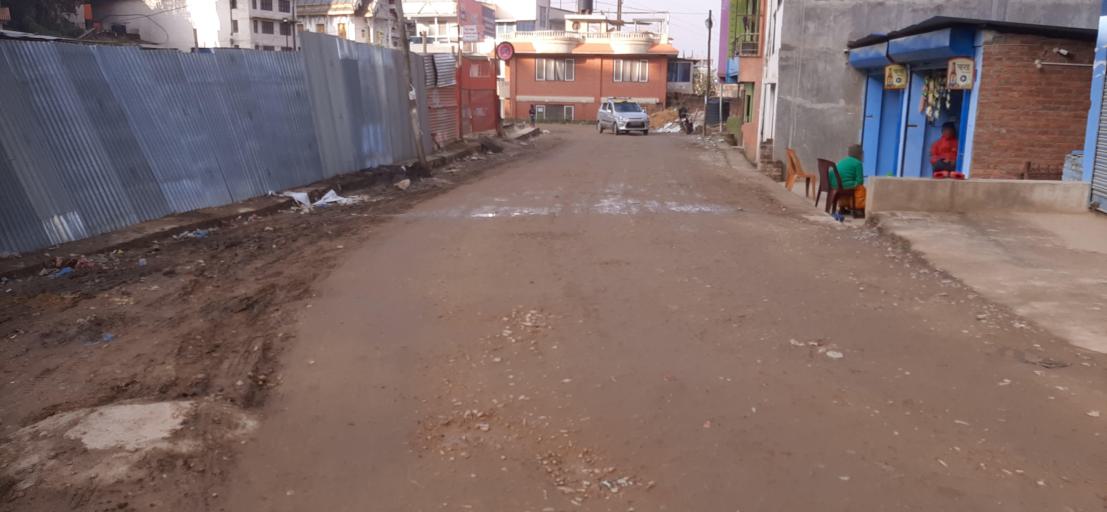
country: NP
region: Central Region
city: Kirtipur
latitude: 27.6741
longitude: 85.2821
